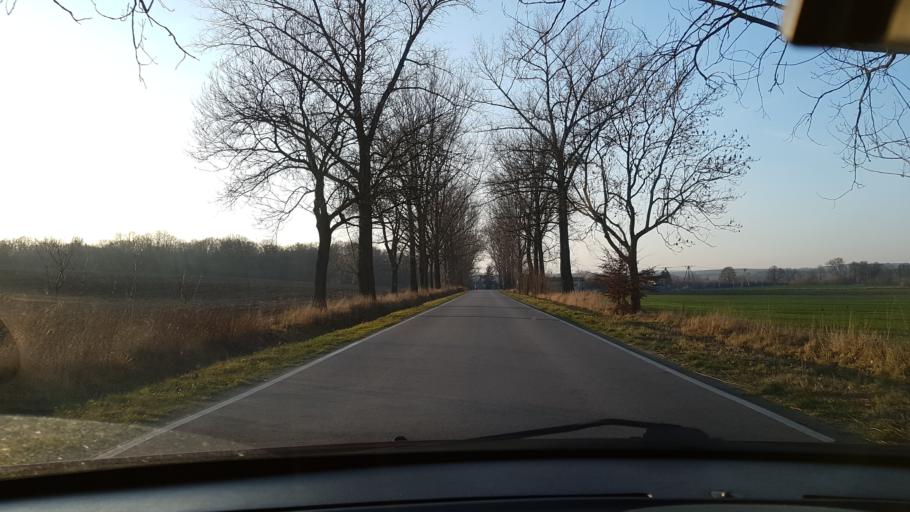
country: PL
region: Lower Silesian Voivodeship
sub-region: Powiat zabkowicki
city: Henrykow
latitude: 50.6589
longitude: 17.0388
